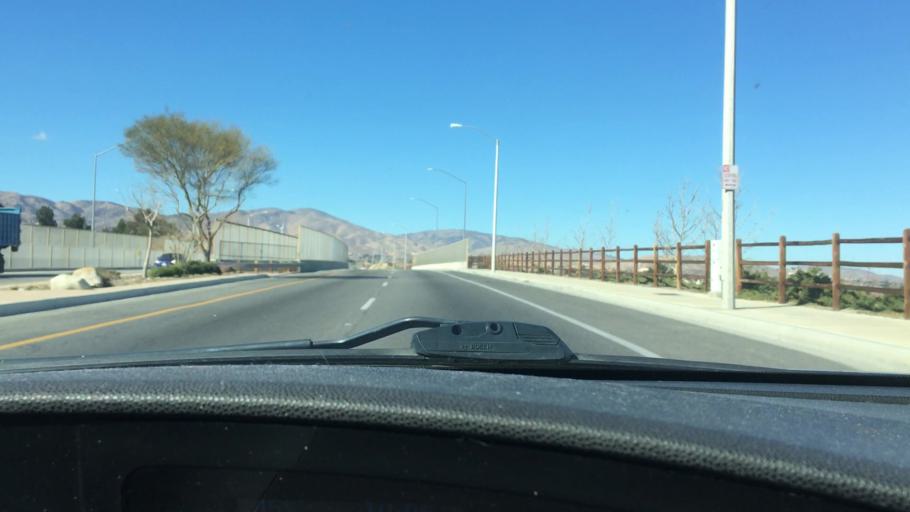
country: US
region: California
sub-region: Los Angeles County
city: Palmdale
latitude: 34.5585
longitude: -118.0954
